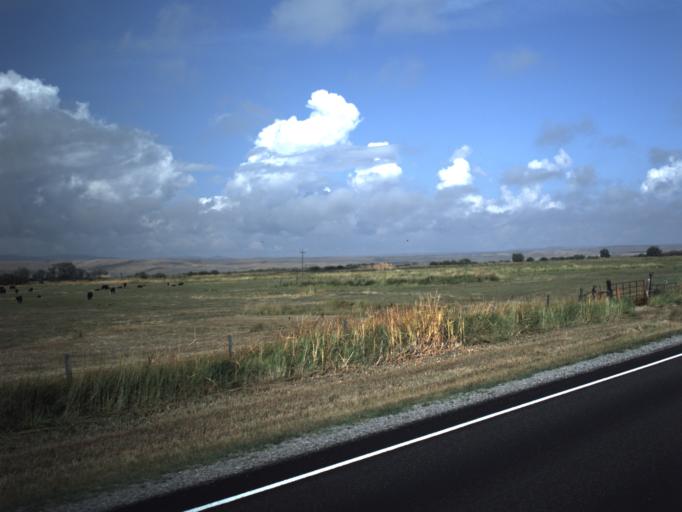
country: US
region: Utah
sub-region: Rich County
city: Randolph
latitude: 41.6230
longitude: -111.1792
